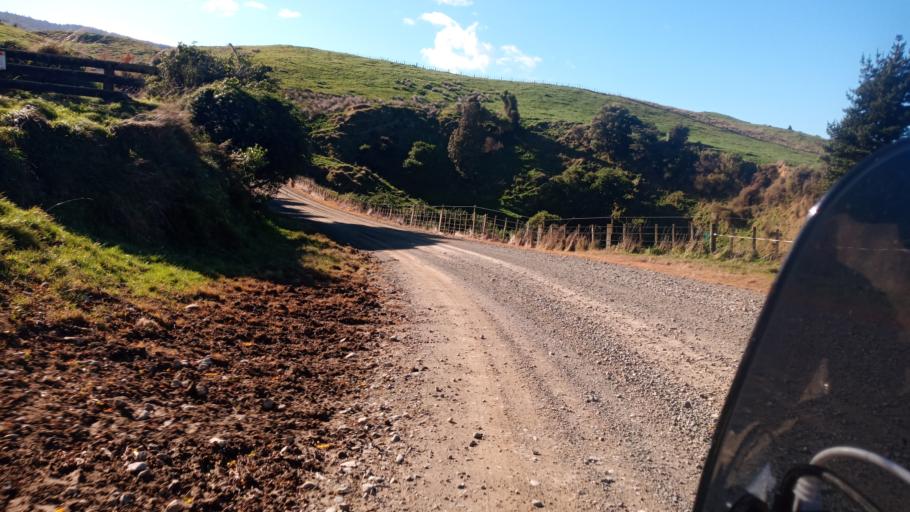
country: NZ
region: Hawke's Bay
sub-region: Wairoa District
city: Wairoa
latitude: -38.7406
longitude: 177.2907
